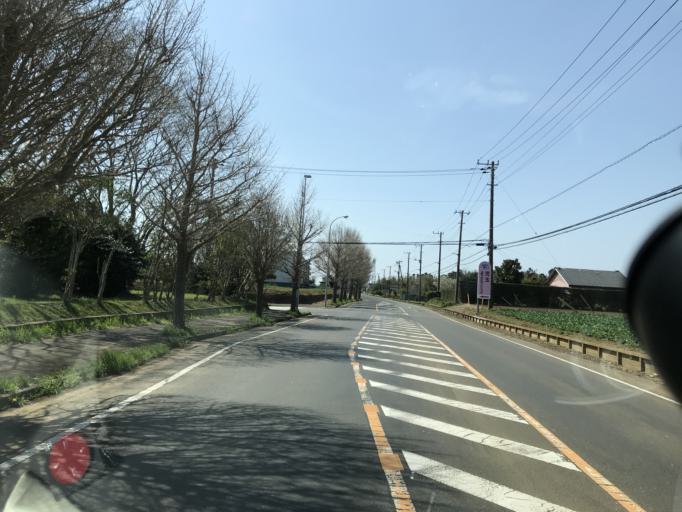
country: JP
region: Chiba
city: Asahi
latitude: 35.7901
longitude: 140.7090
